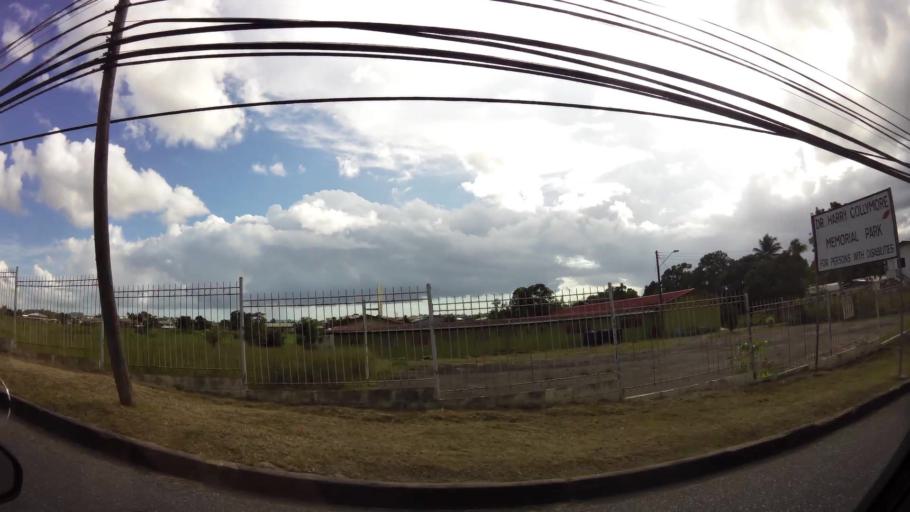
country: TT
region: City of San Fernando
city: Mon Repos
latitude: 10.2671
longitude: -61.4526
